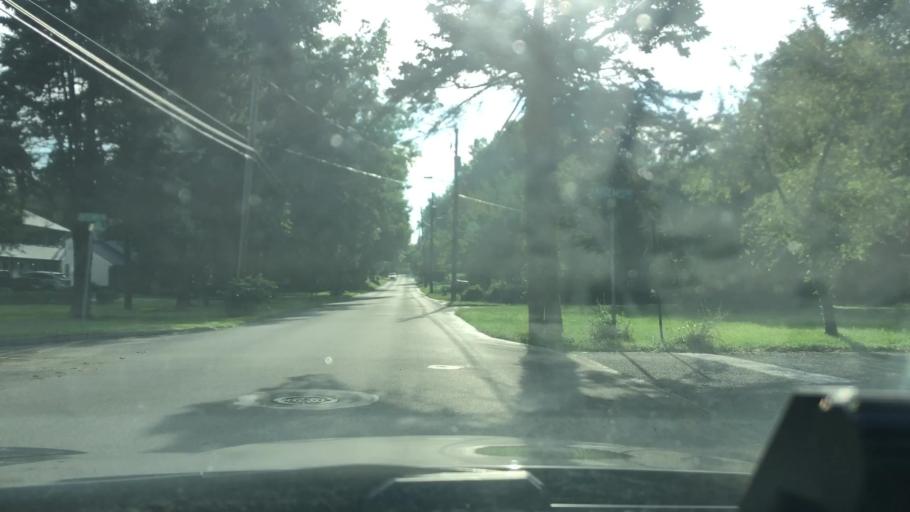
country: US
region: Pennsylvania
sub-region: Northampton County
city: Bethlehem
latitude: 40.6555
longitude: -75.3676
